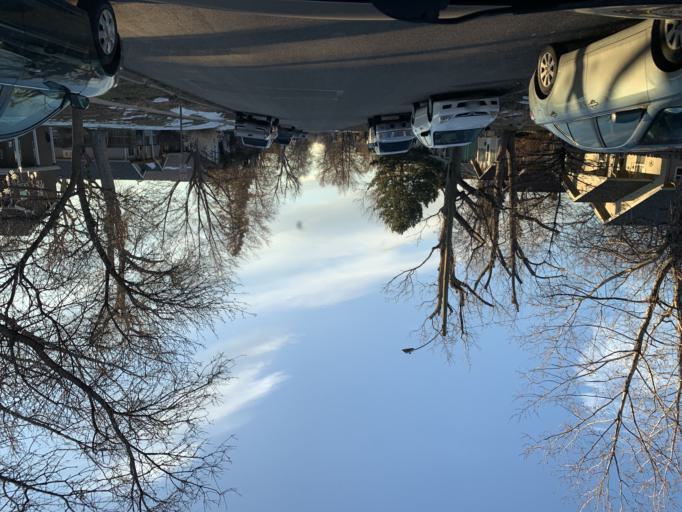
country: US
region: Colorado
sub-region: Adams County
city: Berkley
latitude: 39.7877
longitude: -105.0359
